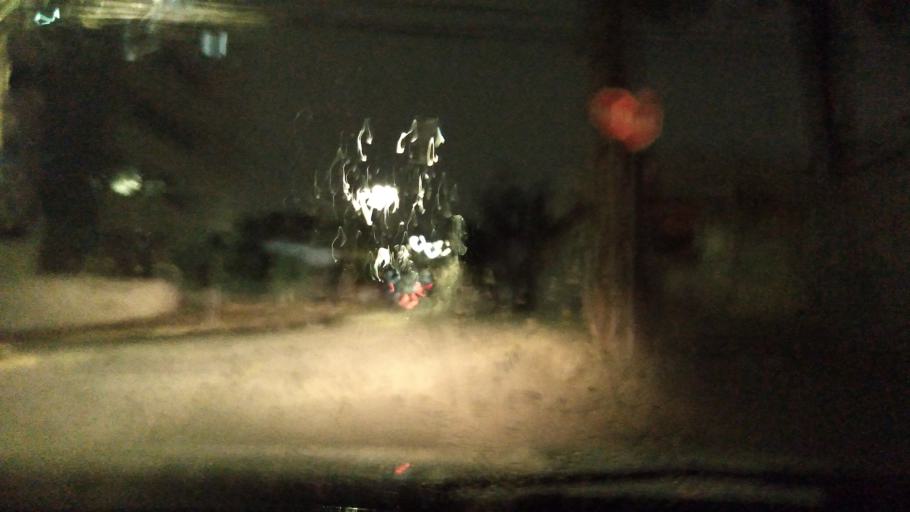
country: BR
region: Minas Gerais
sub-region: Belo Horizonte
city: Belo Horizonte
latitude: -19.8813
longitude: -43.9378
